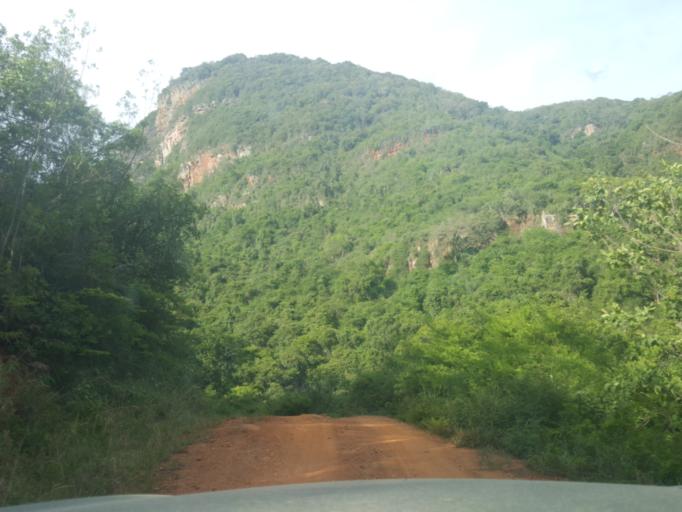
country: ZA
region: Limpopo
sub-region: Mopani District Municipality
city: Hoedspruit
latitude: -24.5906
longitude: 30.8427
